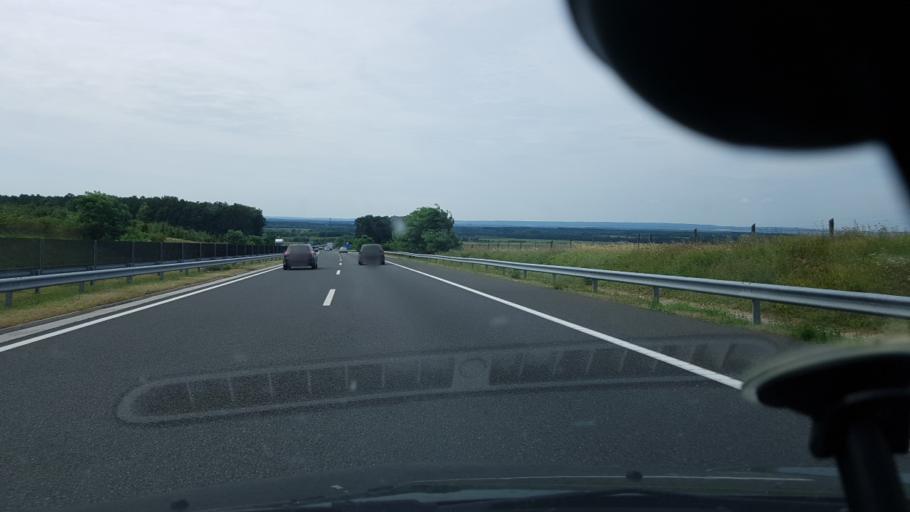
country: HU
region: Somogy
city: Balatonbereny
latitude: 46.6596
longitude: 17.3134
